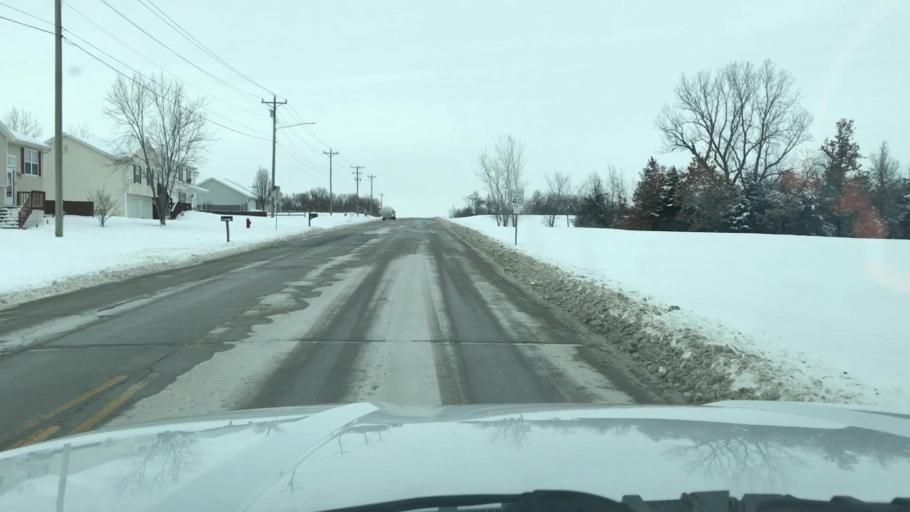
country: US
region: Missouri
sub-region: Clinton County
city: Cameron
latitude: 39.7429
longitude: -94.2153
